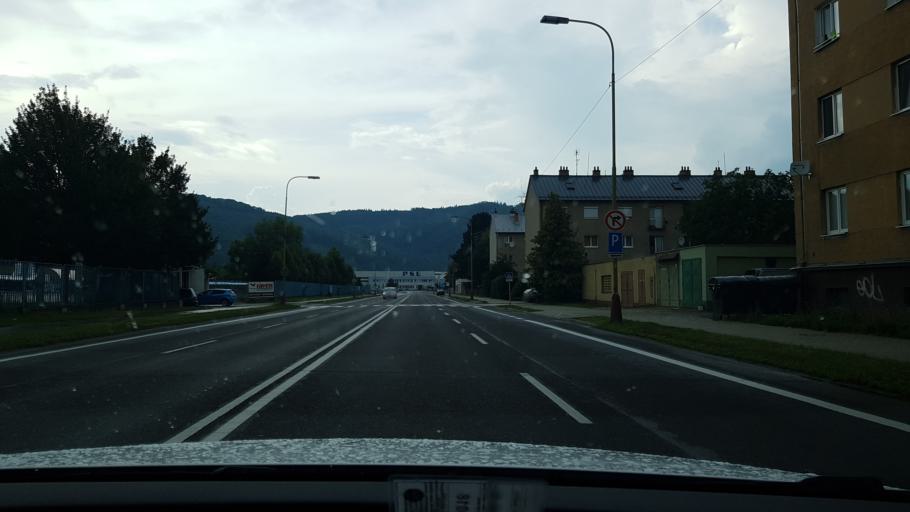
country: SK
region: Trenciansky
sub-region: Okres Povazska Bystrica
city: Povazska Bystrica
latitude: 49.1182
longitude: 18.4293
